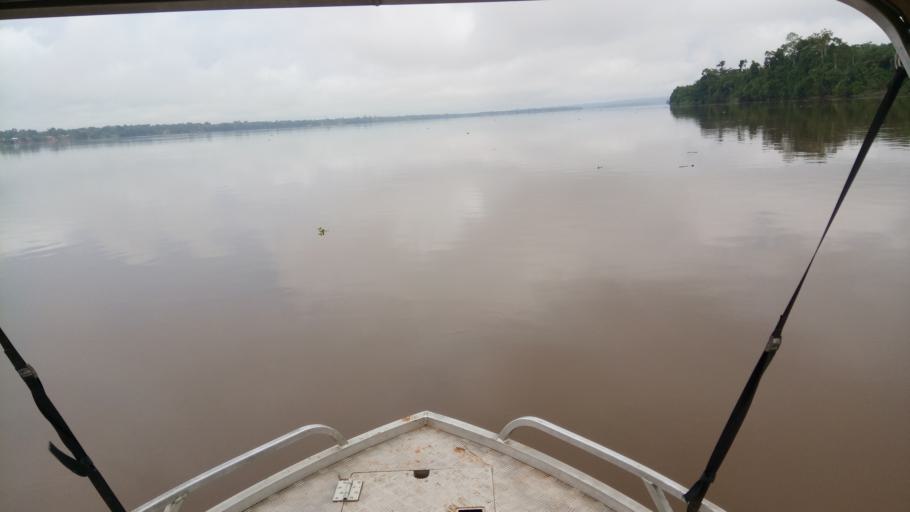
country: CD
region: Eastern Province
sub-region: Sous-Region de la Tshopo
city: Yangambi
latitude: 0.6743
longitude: 24.6057
